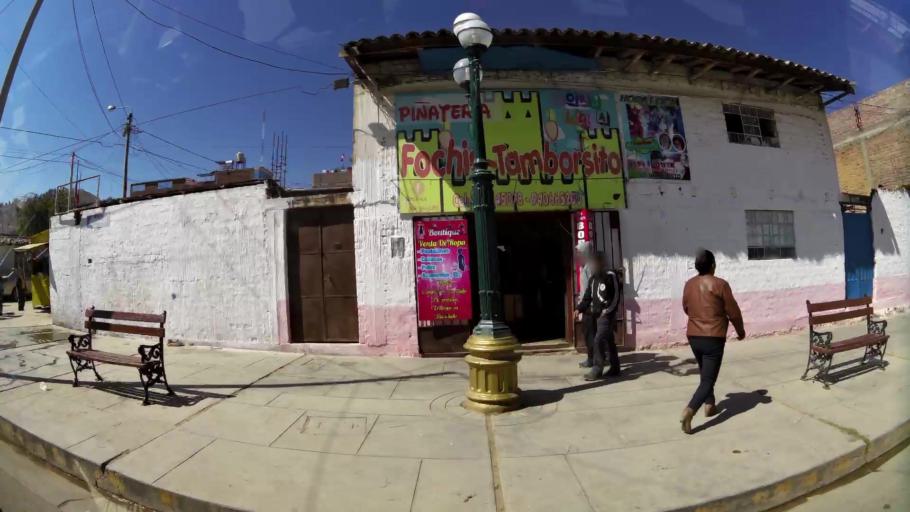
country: PE
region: Junin
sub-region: Provincia de Concepcion
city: Concepcion
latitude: -11.9195
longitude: -75.3140
